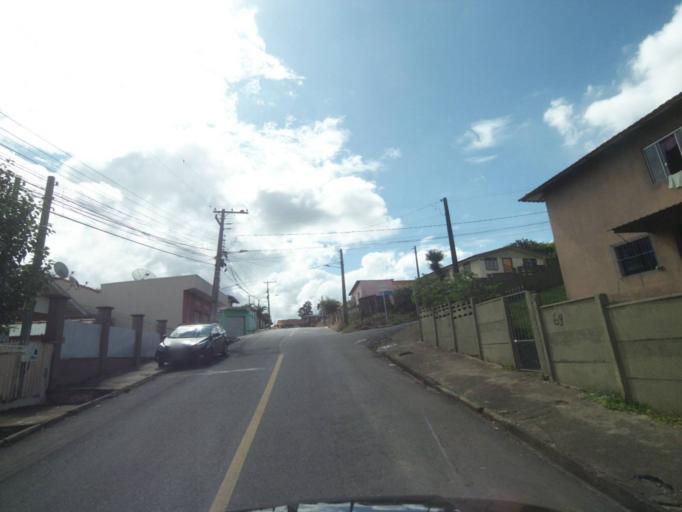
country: BR
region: Parana
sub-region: Telemaco Borba
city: Telemaco Borba
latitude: -24.3181
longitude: -50.6280
